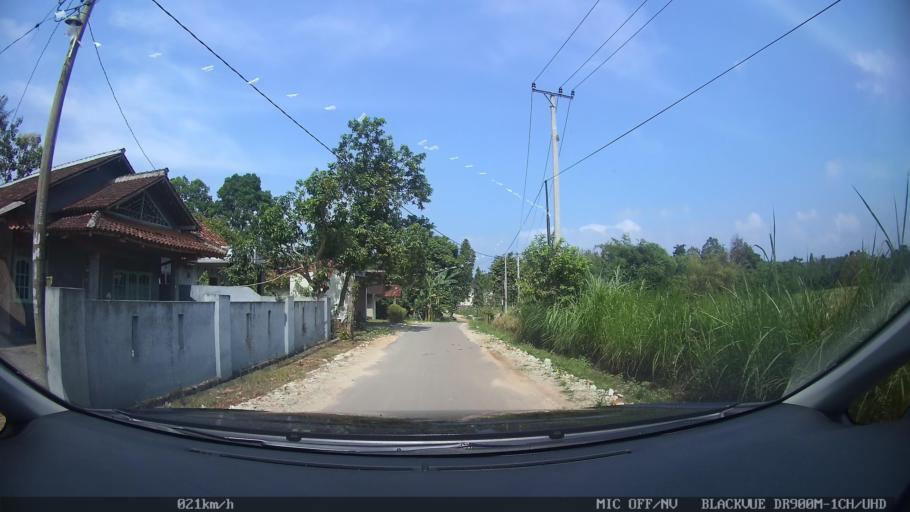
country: ID
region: Lampung
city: Kedaton
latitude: -5.3290
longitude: 105.2740
